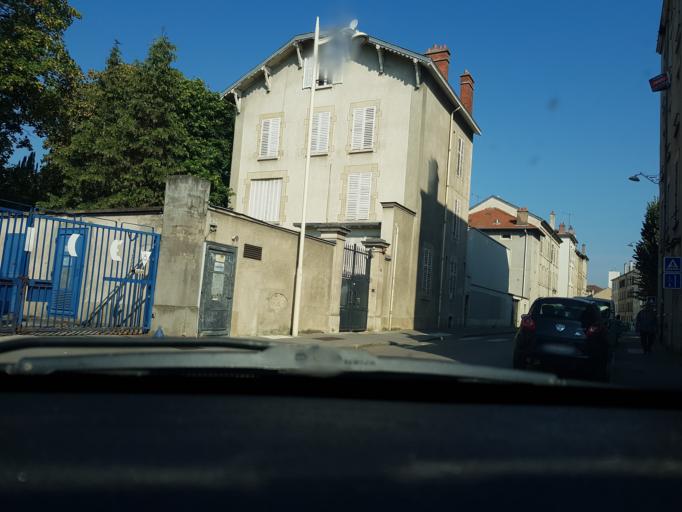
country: FR
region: Lorraine
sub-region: Departement de Meurthe-et-Moselle
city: Nancy
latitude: 48.6830
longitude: 6.1818
